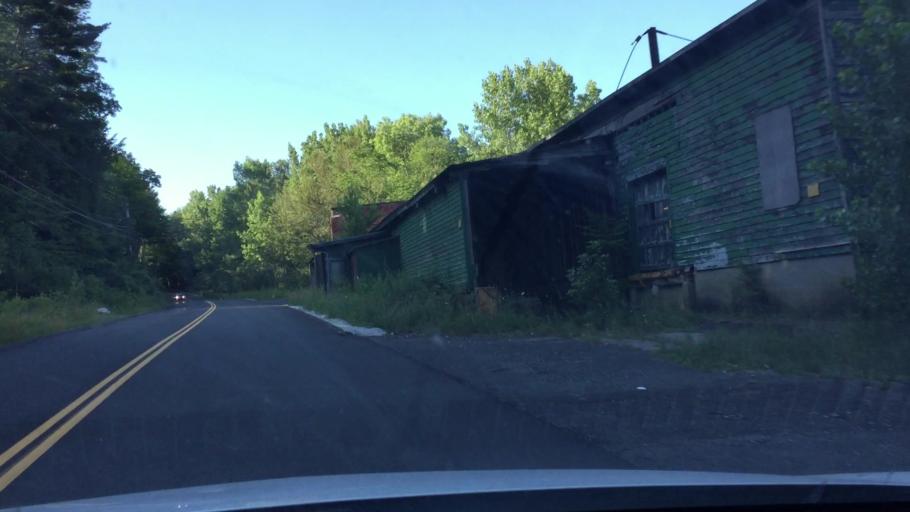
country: US
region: Massachusetts
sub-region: Berkshire County
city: Lee
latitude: 42.2886
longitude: -73.2149
